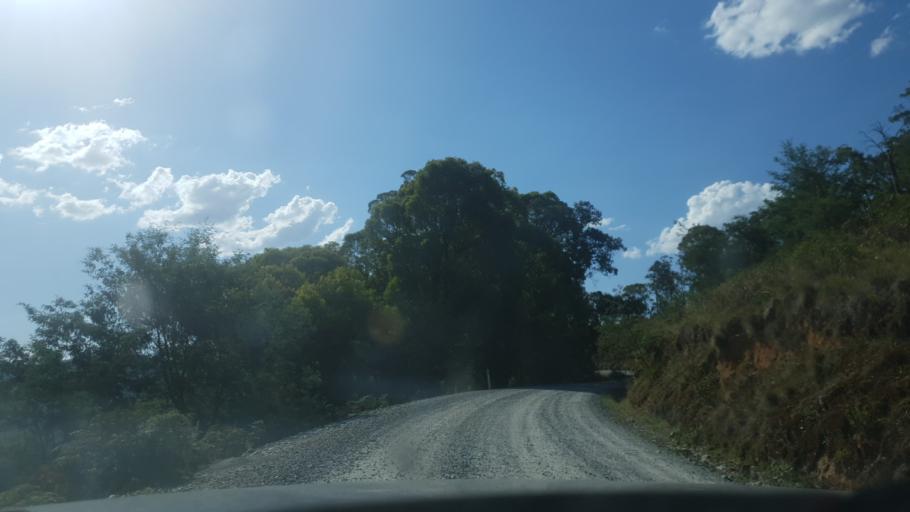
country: AU
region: Victoria
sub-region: Alpine
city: Mount Beauty
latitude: -36.7495
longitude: 147.1814
